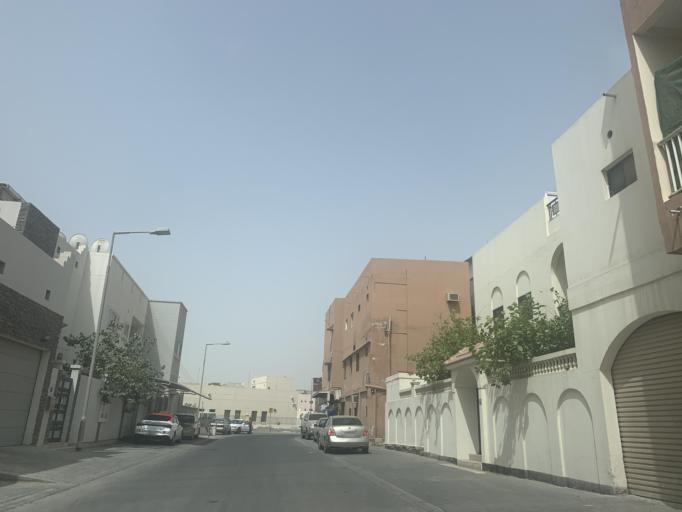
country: BH
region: Manama
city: Jidd Hafs
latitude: 26.2182
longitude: 50.5417
